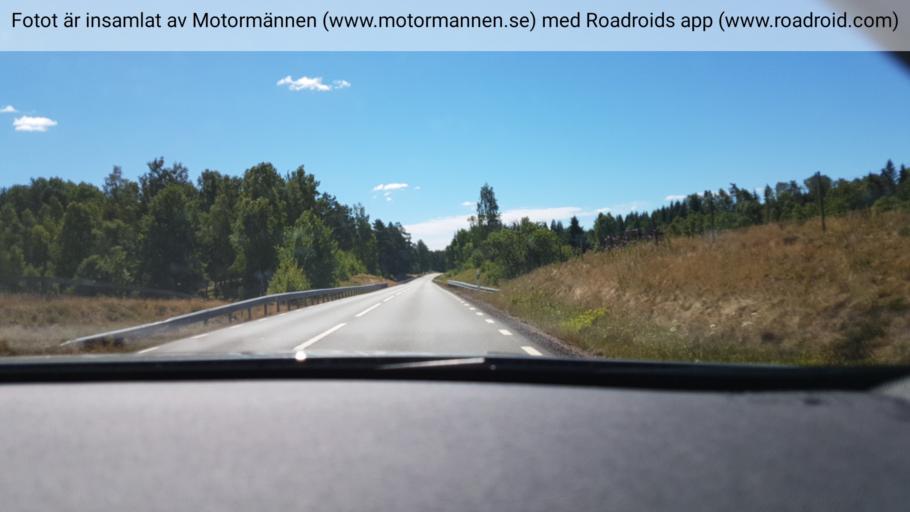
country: SE
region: Joenkoeping
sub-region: Mullsjo Kommun
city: Mullsjoe
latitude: 57.8841
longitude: 13.8488
